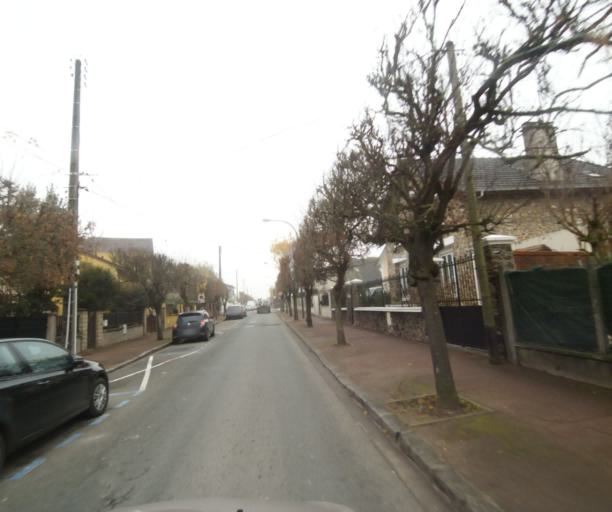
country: FR
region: Ile-de-France
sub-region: Departement de Seine-Saint-Denis
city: Tremblay-en-France
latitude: 48.9412
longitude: 2.5694
